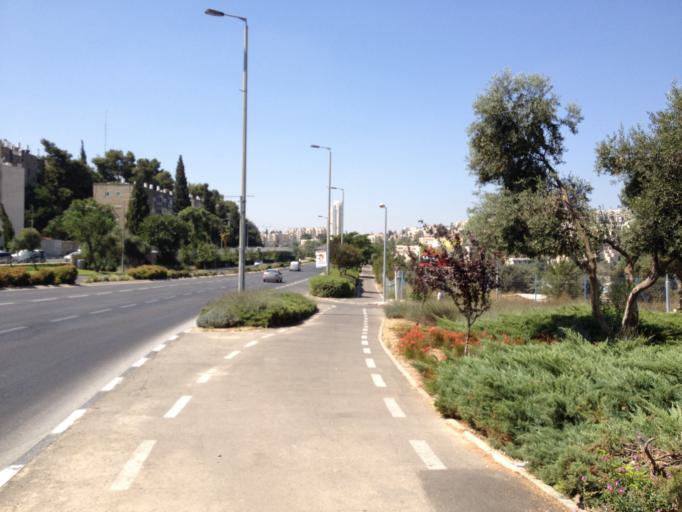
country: IL
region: Jerusalem
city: Jerusalem
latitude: 31.7661
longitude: 35.2039
